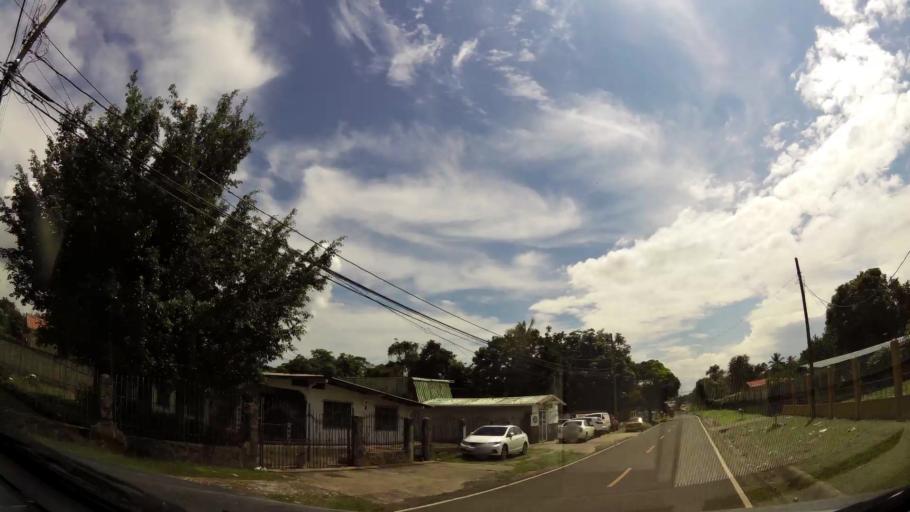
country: PA
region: Panama
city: Vista Alegre
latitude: 8.9300
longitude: -79.7000
